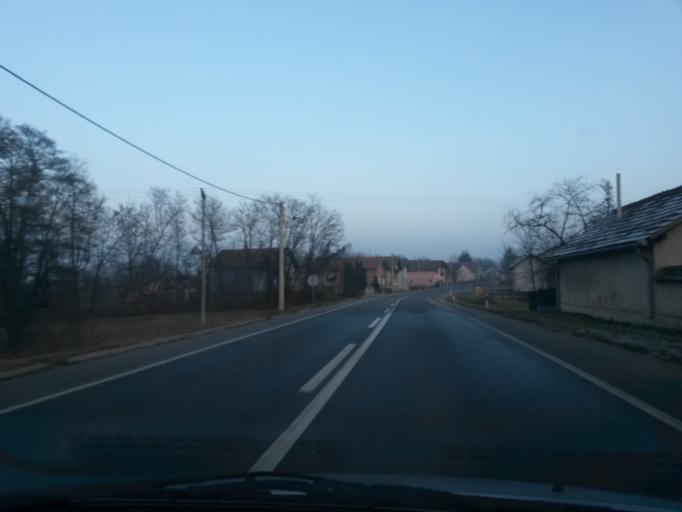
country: HR
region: Varazdinska
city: Ludbreg
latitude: 46.2365
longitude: 16.6443
